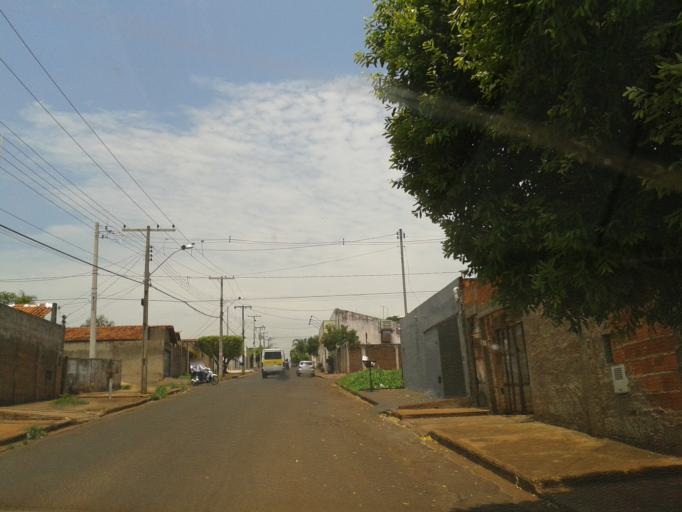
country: BR
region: Minas Gerais
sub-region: Ituiutaba
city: Ituiutaba
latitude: -18.9918
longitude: -49.4427
